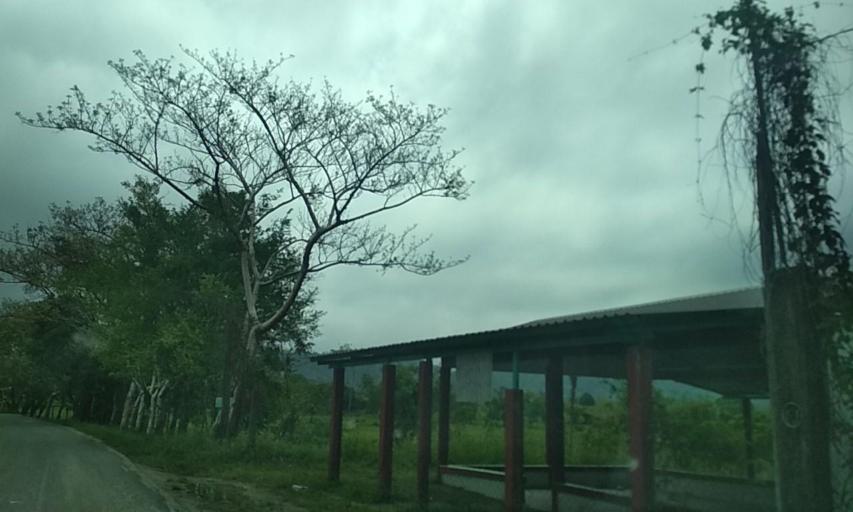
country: MX
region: Veracruz
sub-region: Uxpanapa
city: Poblado 10
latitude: 17.5103
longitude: -94.1572
